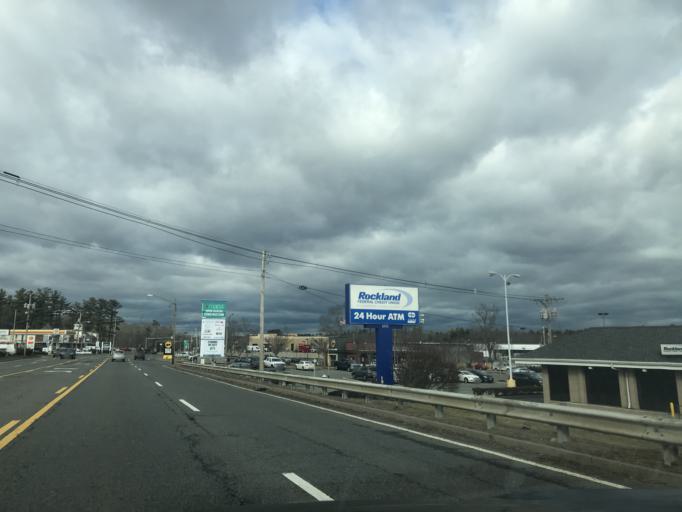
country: US
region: Massachusetts
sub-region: Plymouth County
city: Hanover
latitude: 42.1465
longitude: -70.8451
